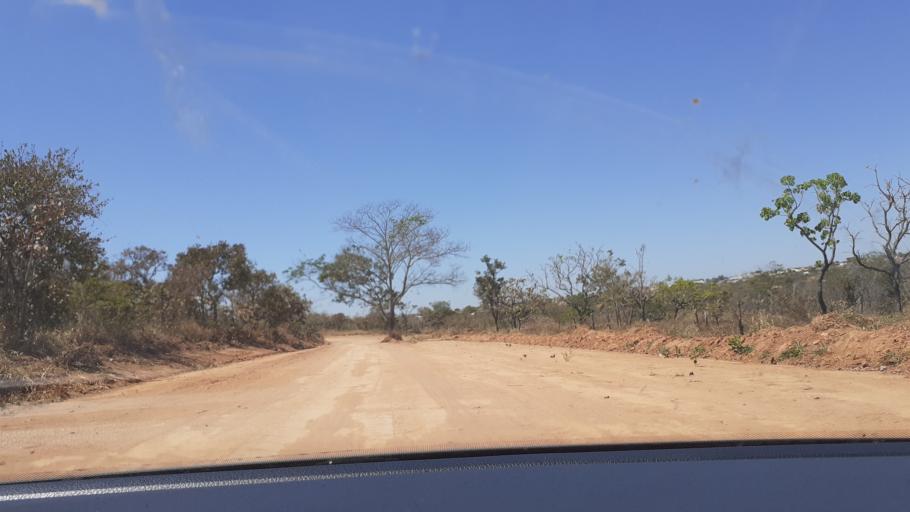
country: BR
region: Goias
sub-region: Caldas Novas
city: Caldas Novas
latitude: -17.7453
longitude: -48.6535
